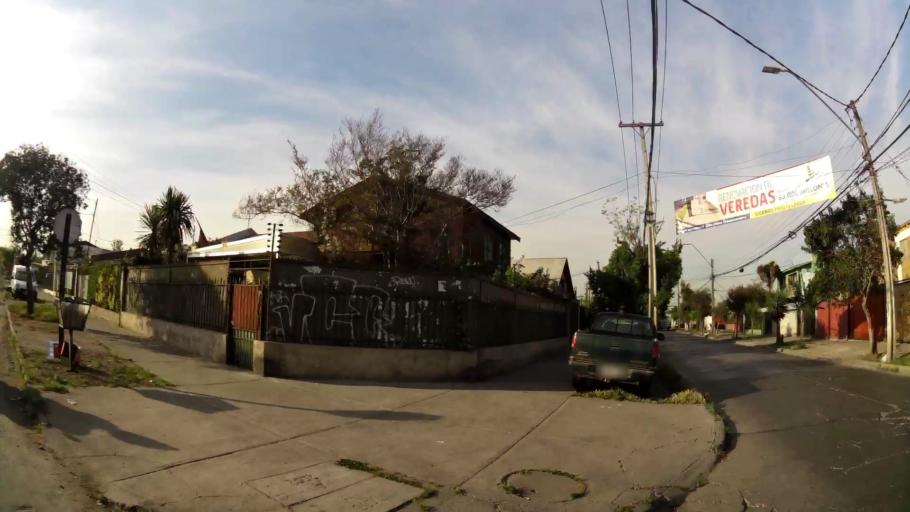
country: CL
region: Santiago Metropolitan
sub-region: Provincia de Santiago
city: Santiago
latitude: -33.5168
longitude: -70.6633
